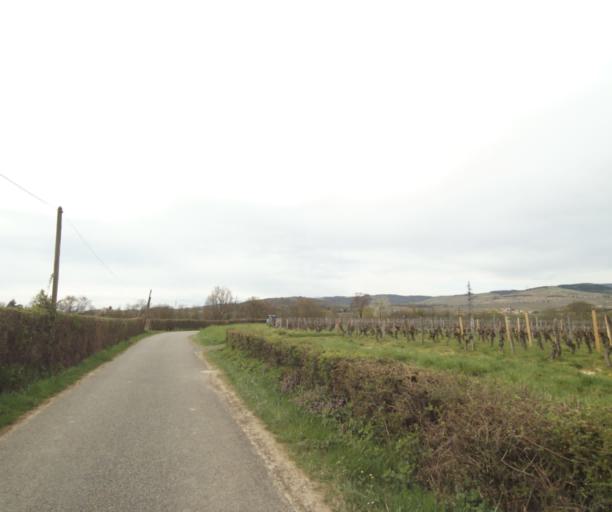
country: FR
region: Bourgogne
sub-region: Departement de Saone-et-Loire
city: Charnay-les-Macon
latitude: 46.3083
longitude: 4.7700
